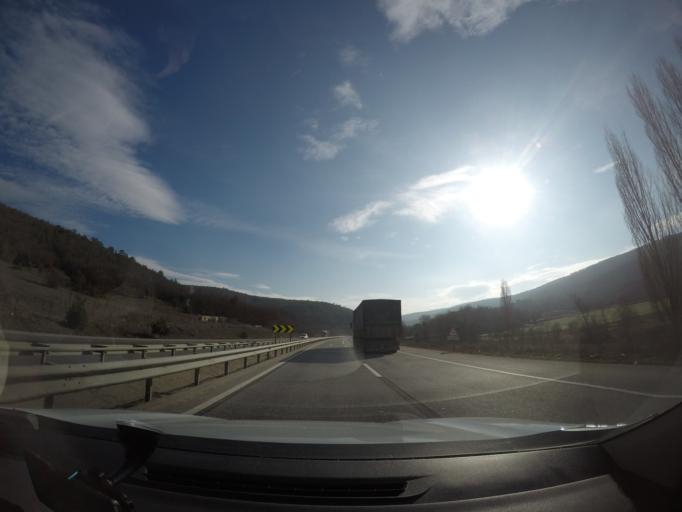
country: TR
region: Bilecik
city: Dodurga
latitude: 39.8901
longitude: 29.9201
